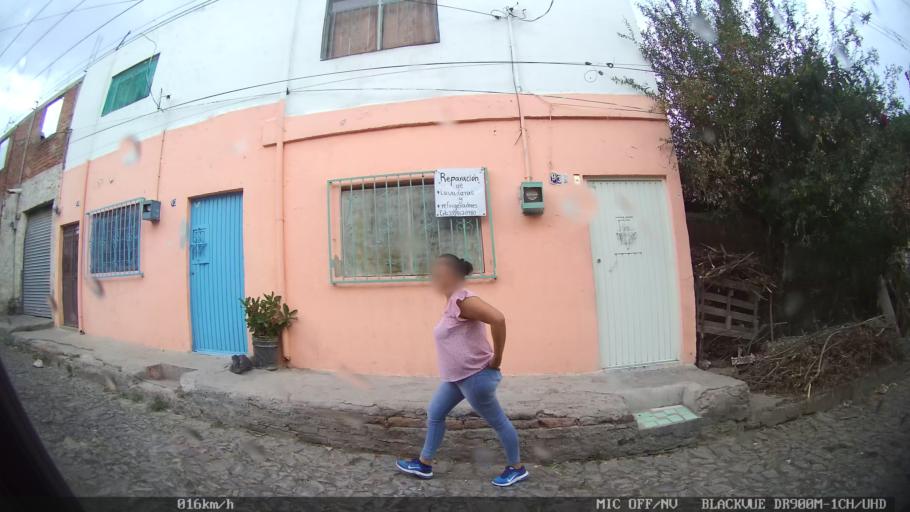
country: MX
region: Jalisco
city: Tonala
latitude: 20.6199
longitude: -103.2665
